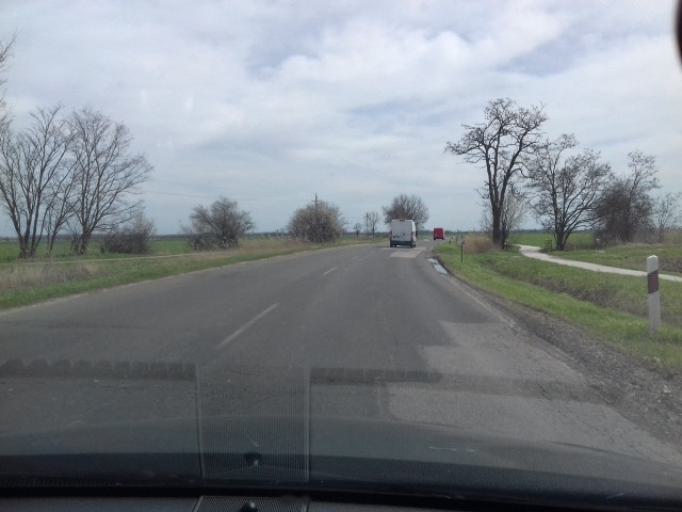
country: HU
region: Jasz-Nagykun-Szolnok
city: Cserkeszolo
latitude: 46.8600
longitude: 20.2217
